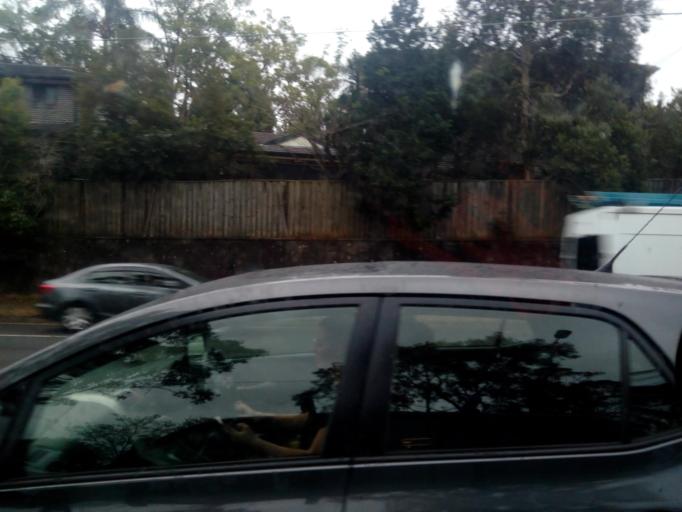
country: AU
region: New South Wales
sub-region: Ku-ring-gai
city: Roseville Chase
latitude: -33.7832
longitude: 151.1929
